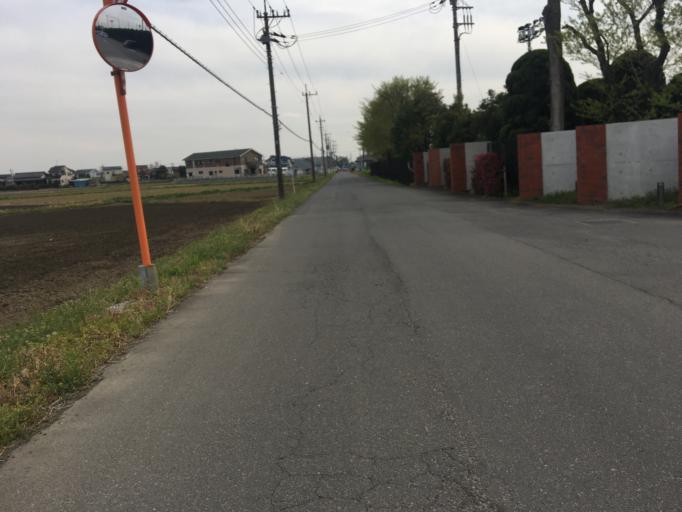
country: JP
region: Saitama
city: Shiki
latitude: 35.8599
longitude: 139.5767
